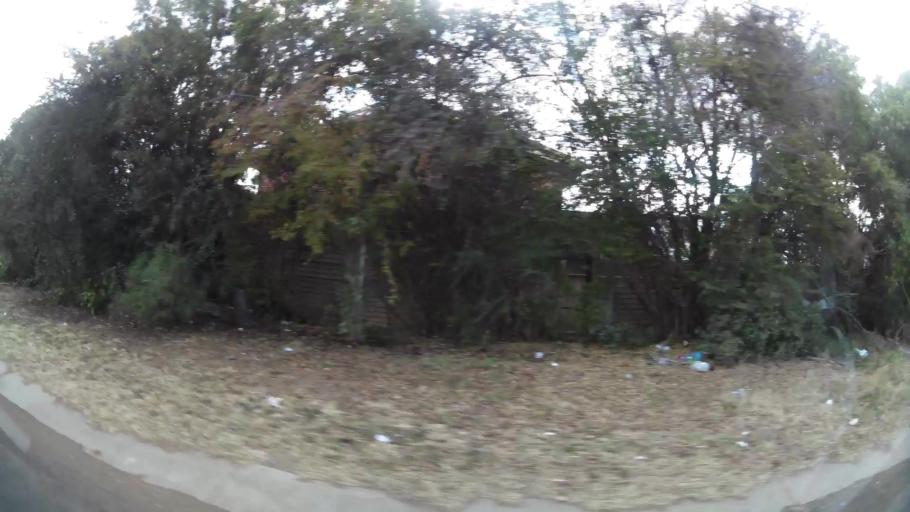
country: ZA
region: Orange Free State
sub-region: Mangaung Metropolitan Municipality
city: Bloemfontein
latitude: -29.0818
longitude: 26.1958
